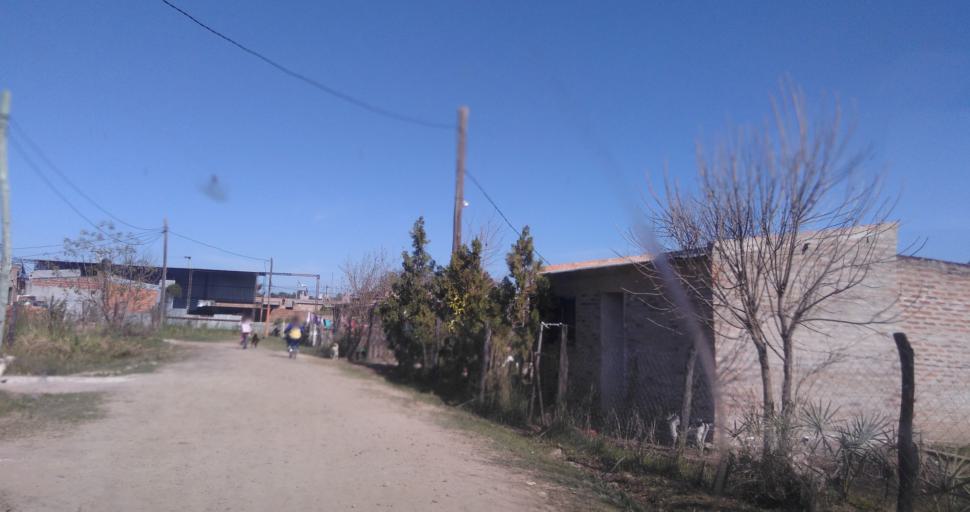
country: AR
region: Chaco
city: Fontana
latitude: -27.4362
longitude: -59.0231
